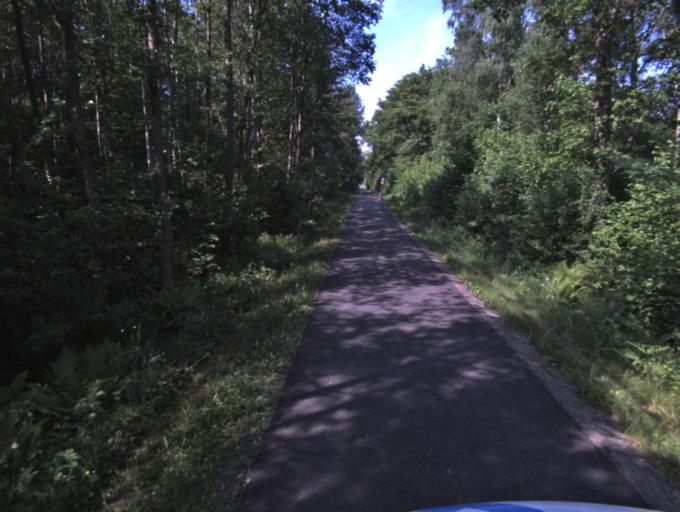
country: SE
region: Skane
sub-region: Kristianstads Kommun
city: Tollarp
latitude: 56.1898
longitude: 14.2881
